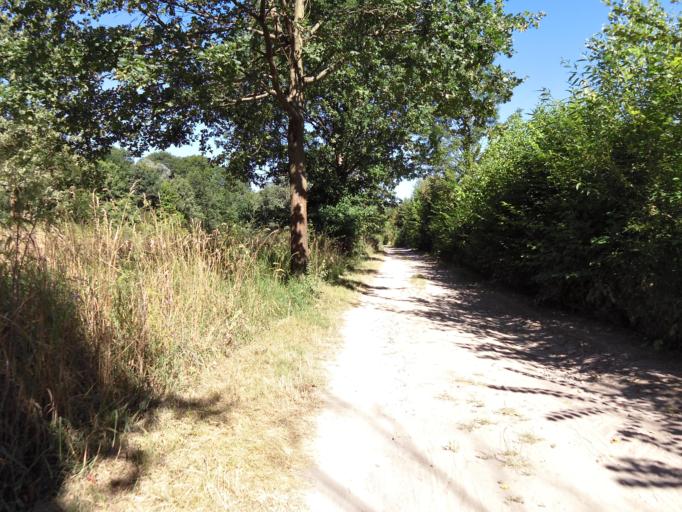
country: DE
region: Rheinland-Pfalz
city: Worms
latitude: 49.6090
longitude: 8.4007
